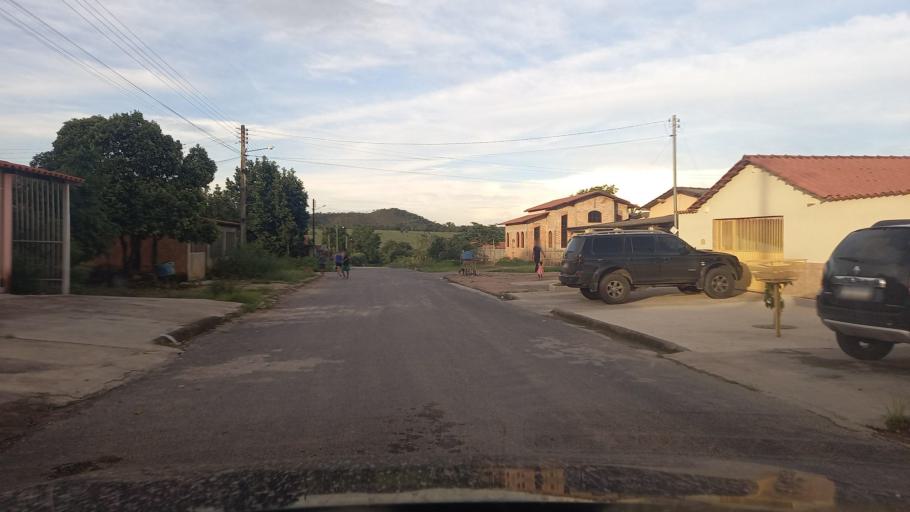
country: BR
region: Goias
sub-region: Cavalcante
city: Cavalcante
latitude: -13.7908
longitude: -47.4548
